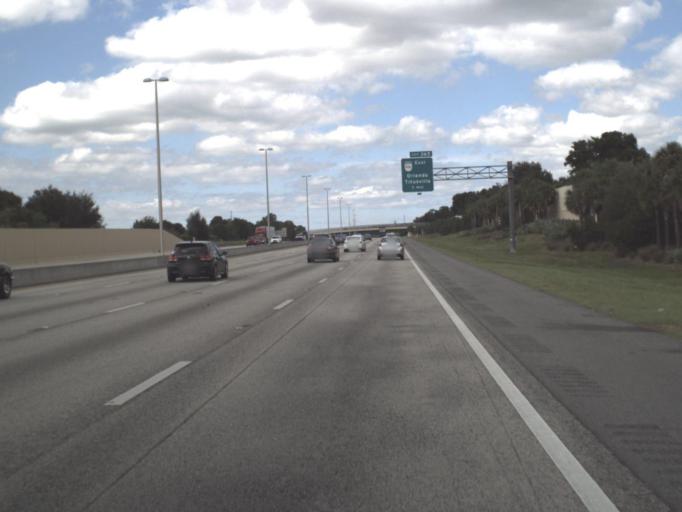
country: US
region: Florida
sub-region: Orange County
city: Gotha
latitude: 28.5243
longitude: -81.5120
